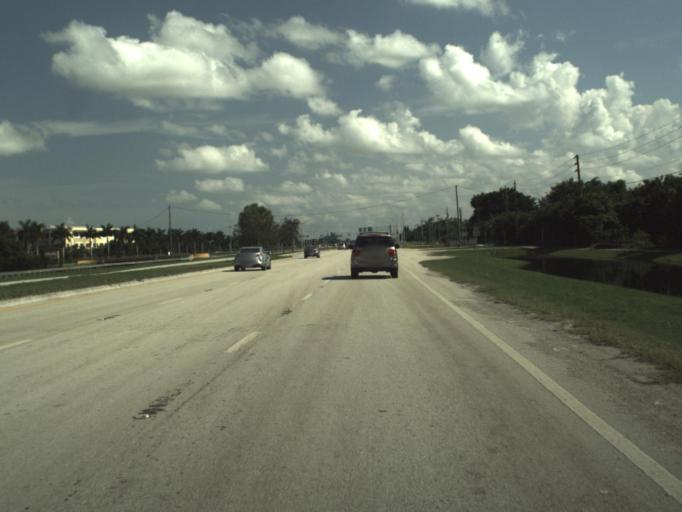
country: US
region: Florida
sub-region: Palm Beach County
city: Villages of Oriole
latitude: 26.5332
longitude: -80.2056
